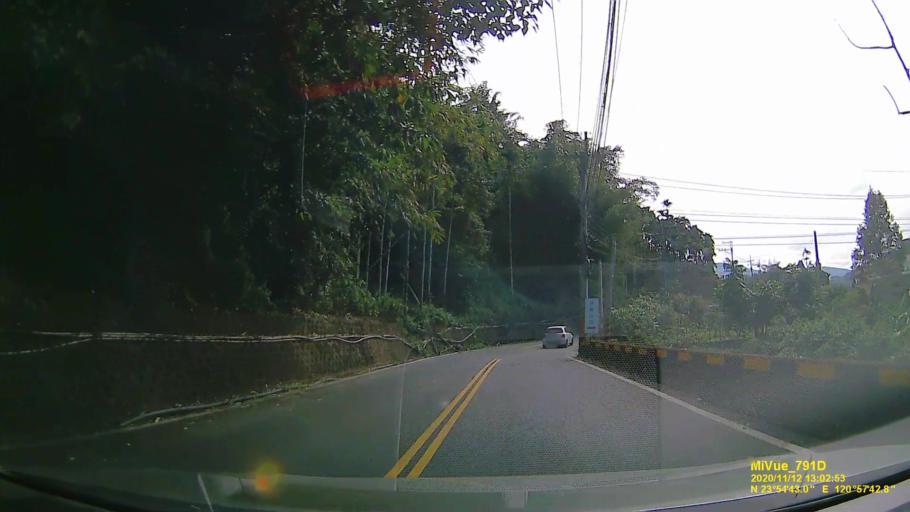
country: TW
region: Taiwan
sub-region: Nantou
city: Puli
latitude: 23.9119
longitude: 120.9619
